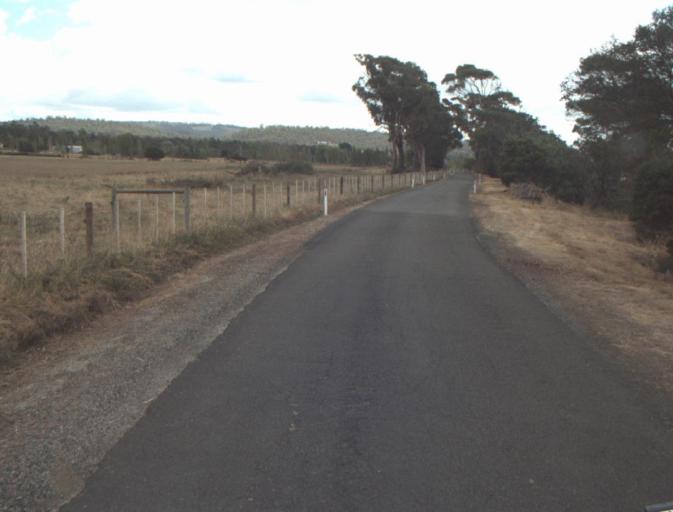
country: AU
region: Tasmania
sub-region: Launceston
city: Mayfield
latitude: -41.2856
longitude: 146.9995
